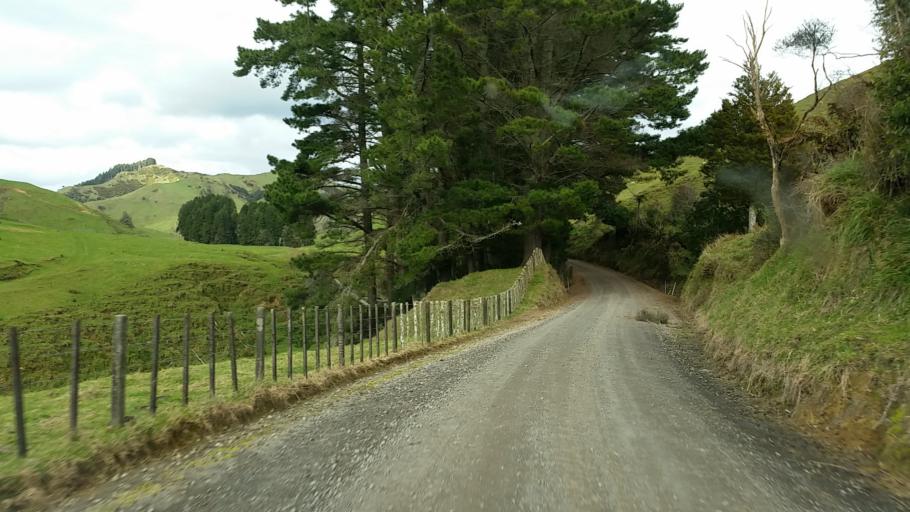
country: NZ
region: Taranaki
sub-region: New Plymouth District
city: Waitara
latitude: -39.1628
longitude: 174.5968
